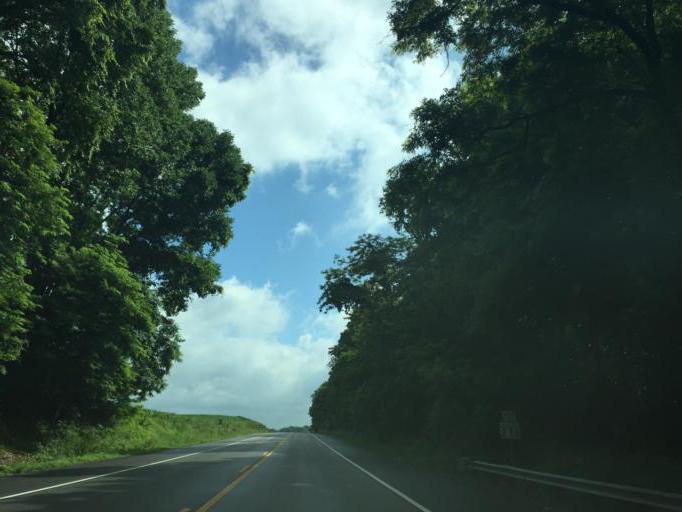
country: US
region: Maryland
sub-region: Cecil County
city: Rising Sun
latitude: 39.6998
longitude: -76.0862
